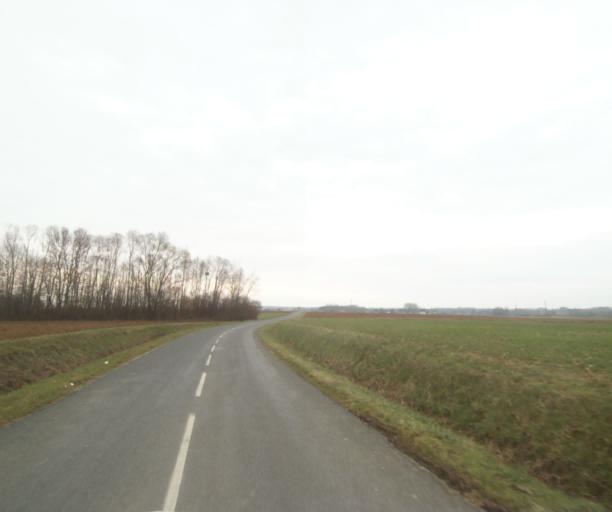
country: FR
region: Champagne-Ardenne
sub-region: Departement de la Haute-Marne
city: Villiers-en-Lieu
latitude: 48.6299
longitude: 4.7731
